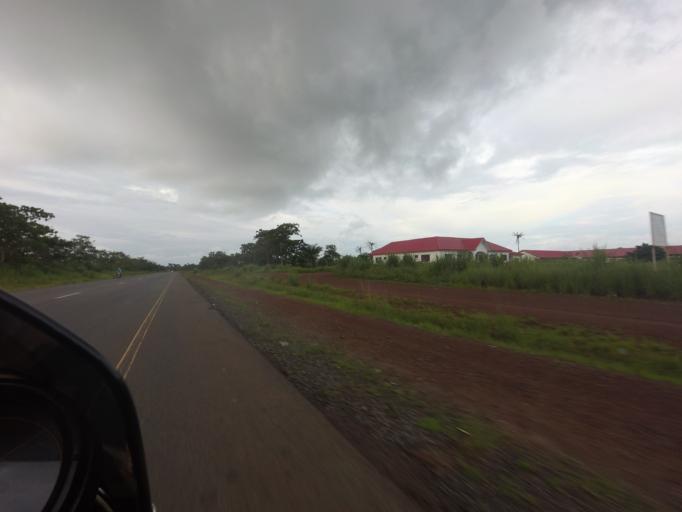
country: SL
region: Northern Province
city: Kambia
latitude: 9.0833
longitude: -12.9116
